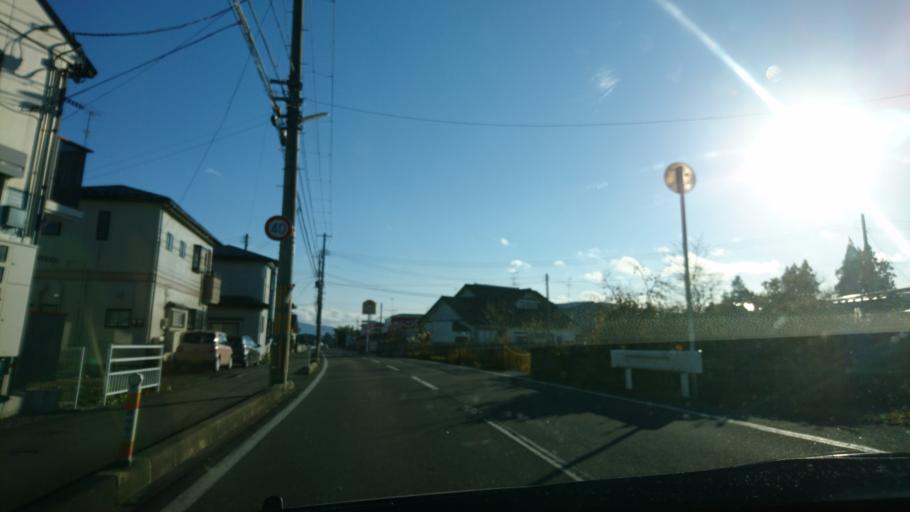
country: JP
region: Iwate
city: Mizusawa
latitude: 39.1248
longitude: 141.1556
